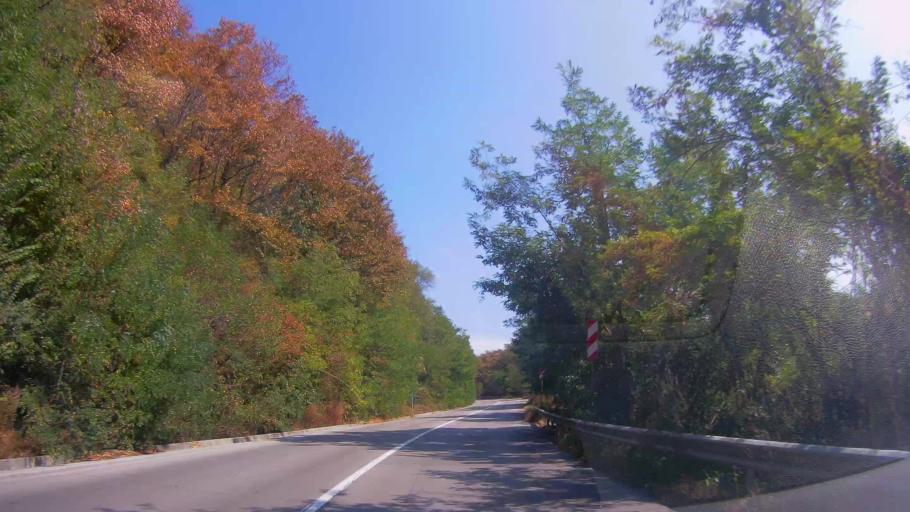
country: BG
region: Shumen
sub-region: Obshtina Smyadovo
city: Smyadovo
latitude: 42.9883
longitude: 27.0395
